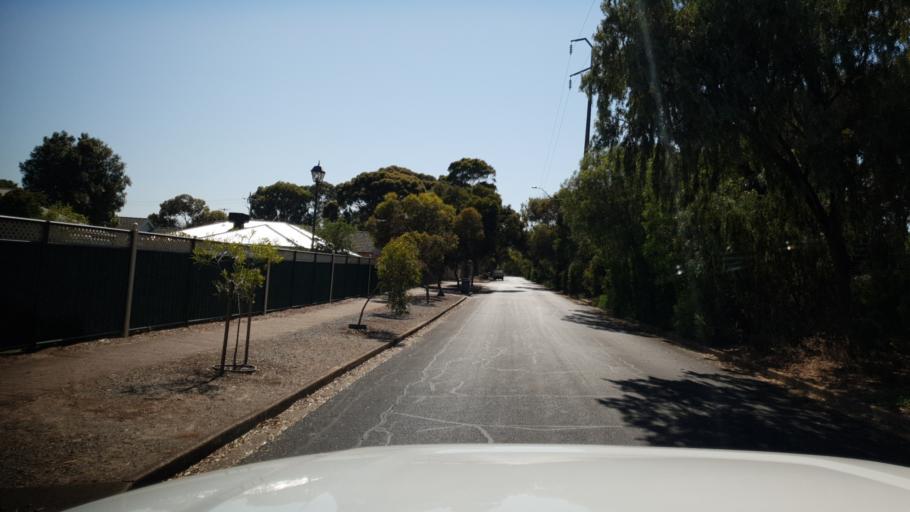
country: AU
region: South Australia
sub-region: Marion
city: Clovelly Park
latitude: -34.9961
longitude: 138.5847
